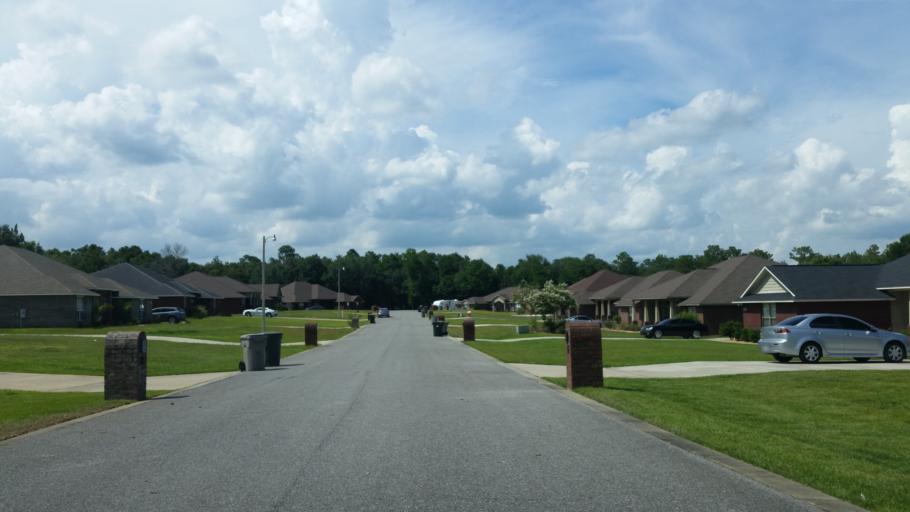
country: US
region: Florida
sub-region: Escambia County
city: Cantonment
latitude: 30.5518
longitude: -87.3831
